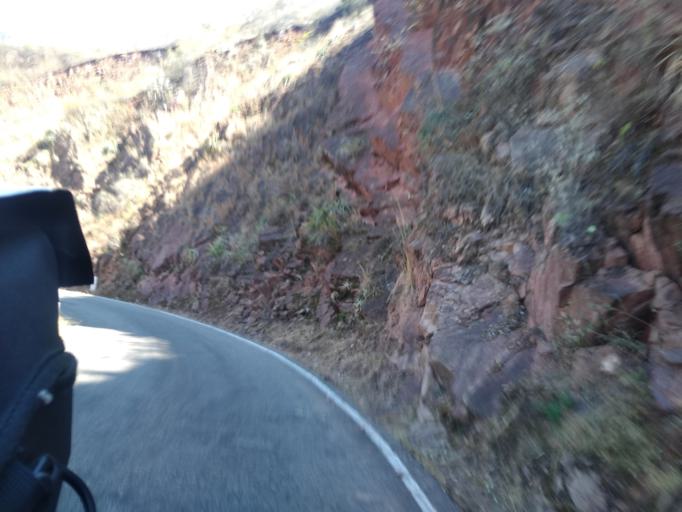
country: PE
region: Amazonas
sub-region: Provincia de Chachapoyas
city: Balsas
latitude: -6.8476
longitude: -77.9662
